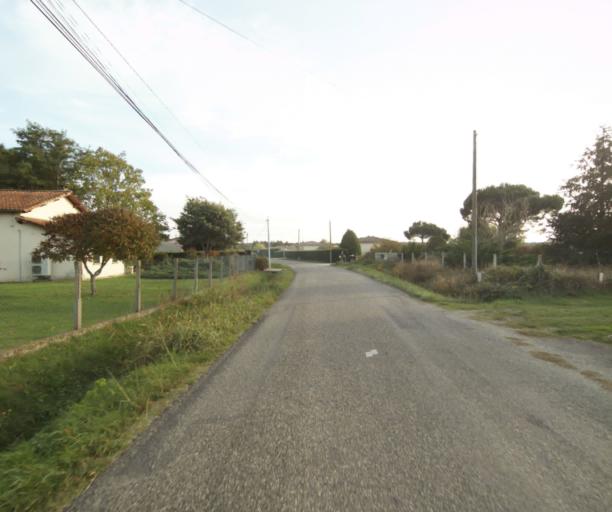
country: FR
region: Midi-Pyrenees
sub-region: Departement du Tarn-et-Garonne
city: Campsas
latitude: 43.8865
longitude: 1.3344
